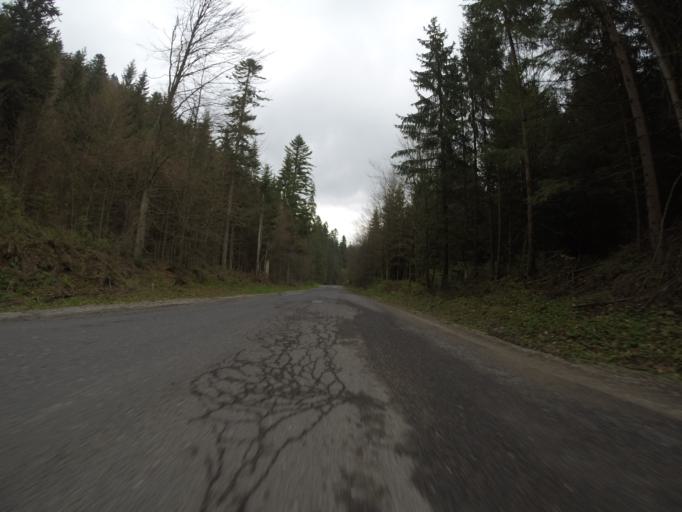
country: SK
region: Banskobystricky
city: Revuca
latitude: 48.7972
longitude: 20.1390
